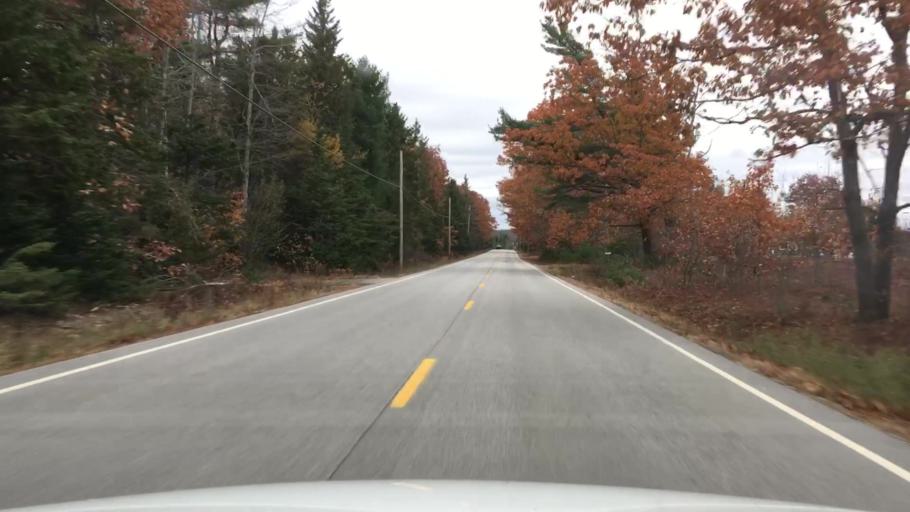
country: US
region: Maine
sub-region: Hancock County
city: Penobscot
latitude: 44.4882
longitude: -68.6423
